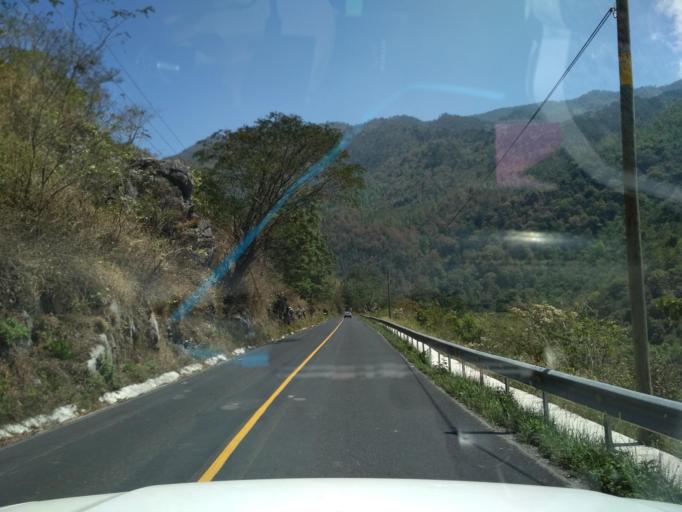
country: MX
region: Veracruz
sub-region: Tlilapan
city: Tonalixco
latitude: 18.7631
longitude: -97.0836
